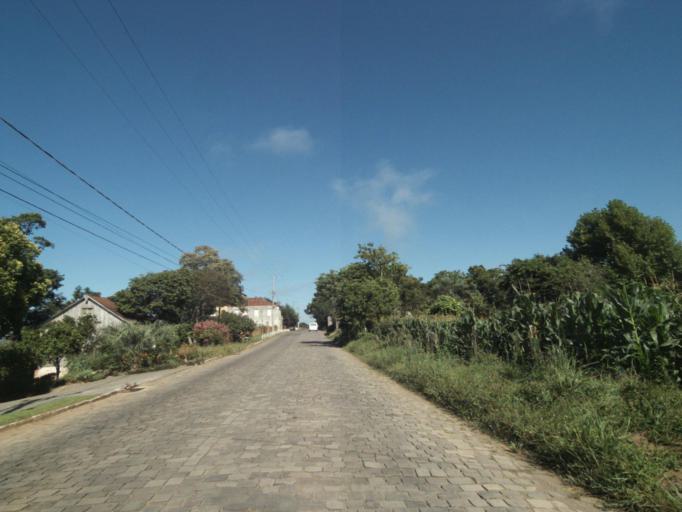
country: BR
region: Rio Grande do Sul
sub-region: Bento Goncalves
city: Bento Goncalves
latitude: -29.1183
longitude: -51.5684
